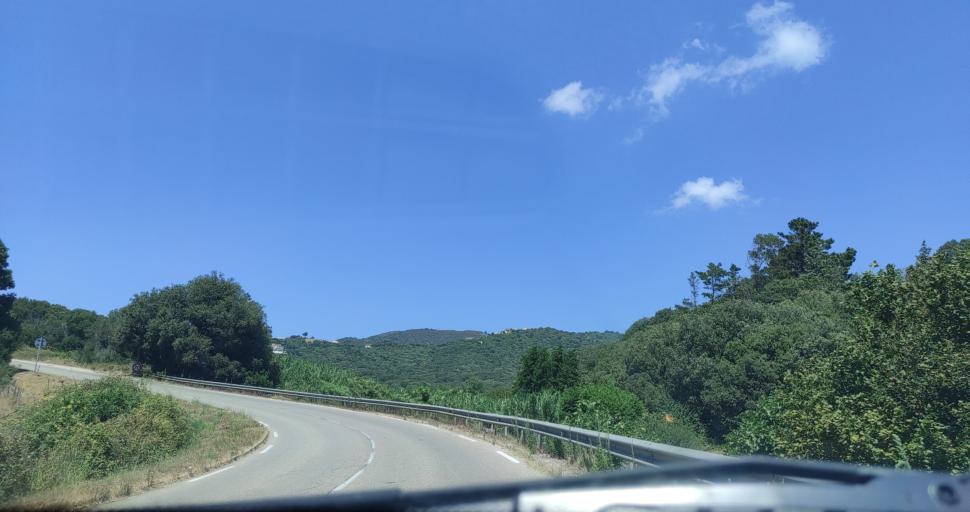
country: FR
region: Corsica
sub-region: Departement de la Corse-du-Sud
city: Ajaccio
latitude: 41.9528
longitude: 8.7324
